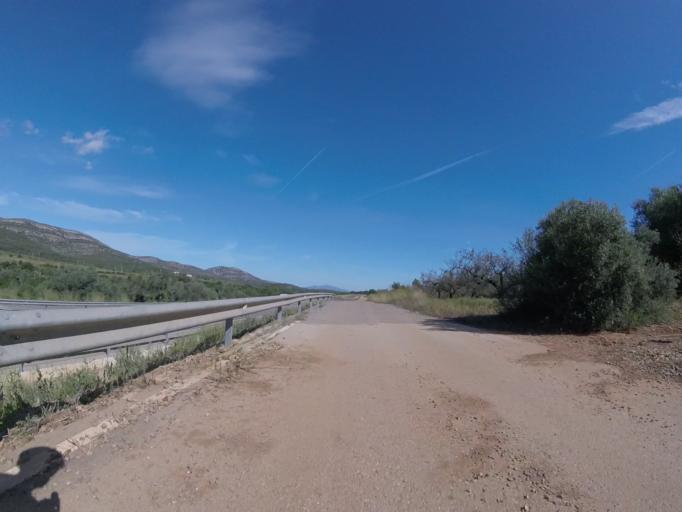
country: ES
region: Valencia
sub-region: Provincia de Castello
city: Santa Magdalena de Pulpis
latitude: 40.3732
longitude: 0.3276
